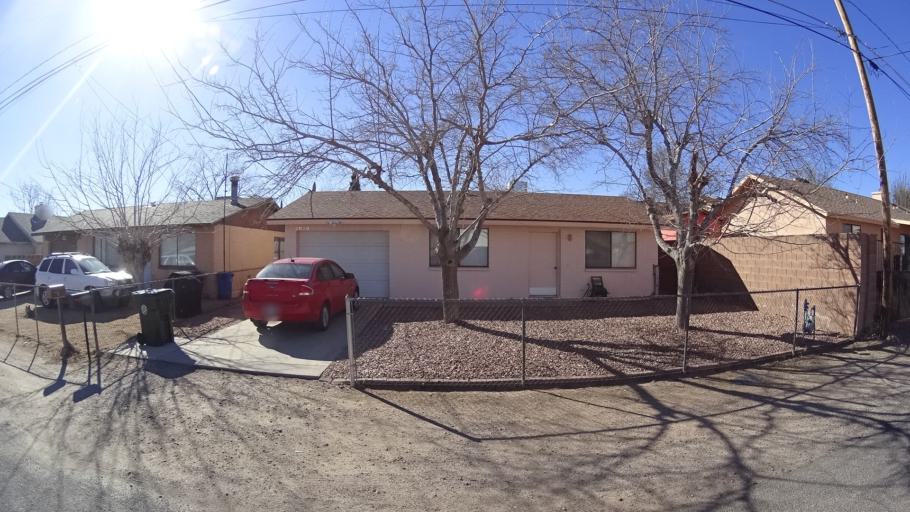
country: US
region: Arizona
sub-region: Mohave County
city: Kingman
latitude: 35.2009
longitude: -114.0309
